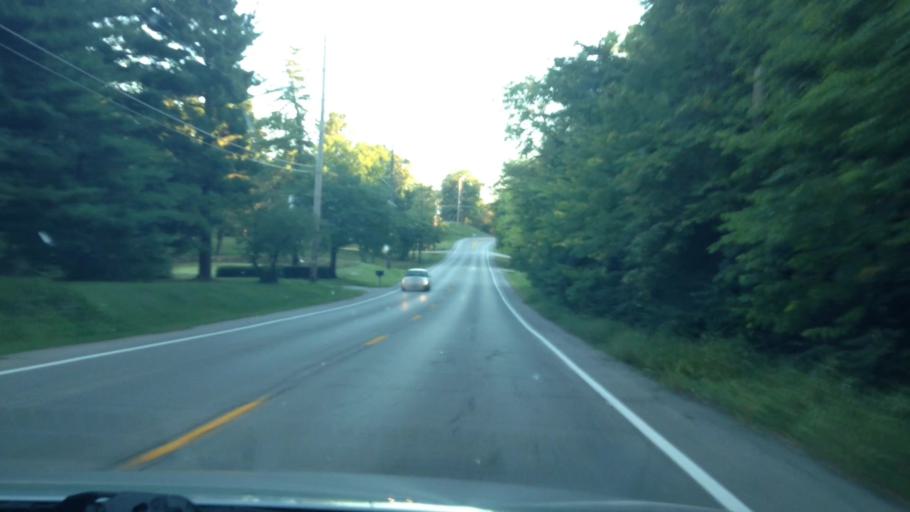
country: US
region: Missouri
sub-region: Platte County
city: Weatherby Lake
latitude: 39.2293
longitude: -94.6590
